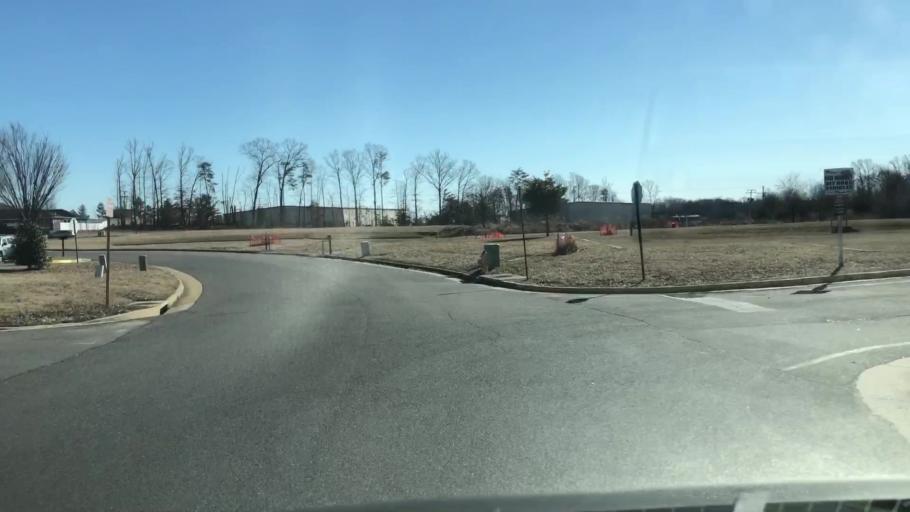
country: US
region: Virginia
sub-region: Stafford County
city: Falmouth
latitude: 38.3543
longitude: -77.5039
